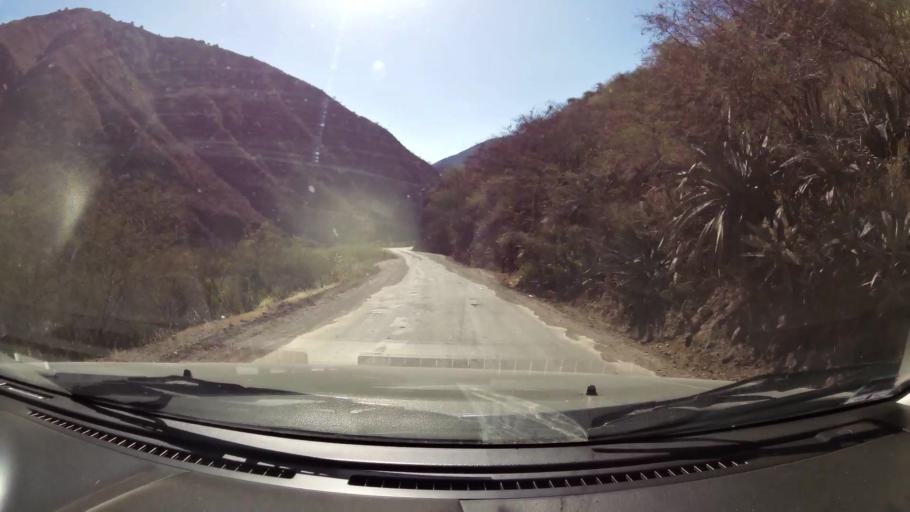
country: PE
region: Huancavelica
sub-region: Provincia de Acobamba
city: Pomacocha
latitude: -12.7777
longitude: -74.4981
